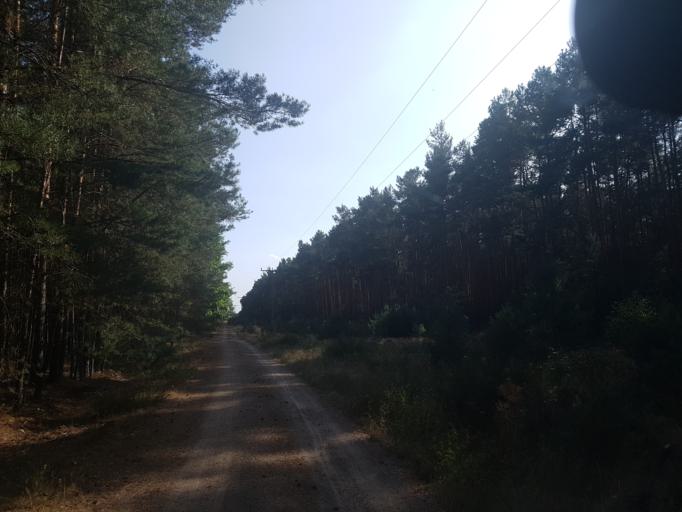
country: DE
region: Saxony-Anhalt
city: Jessen
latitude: 51.8634
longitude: 13.0331
